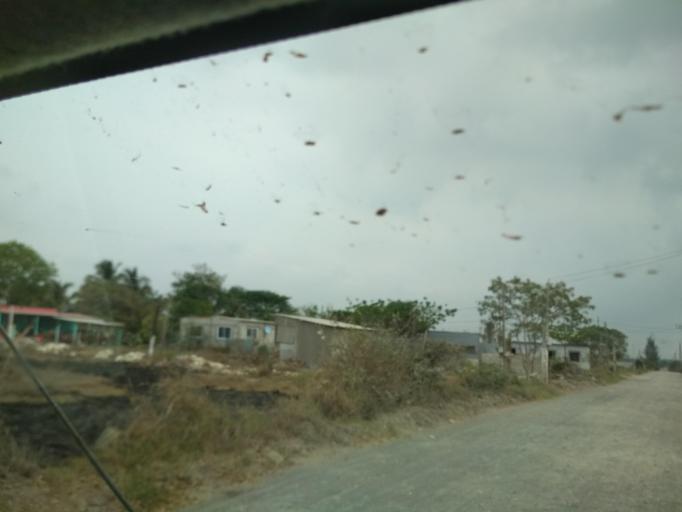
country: MX
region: Veracruz
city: Paso del Toro
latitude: 19.0113
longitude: -96.1109
